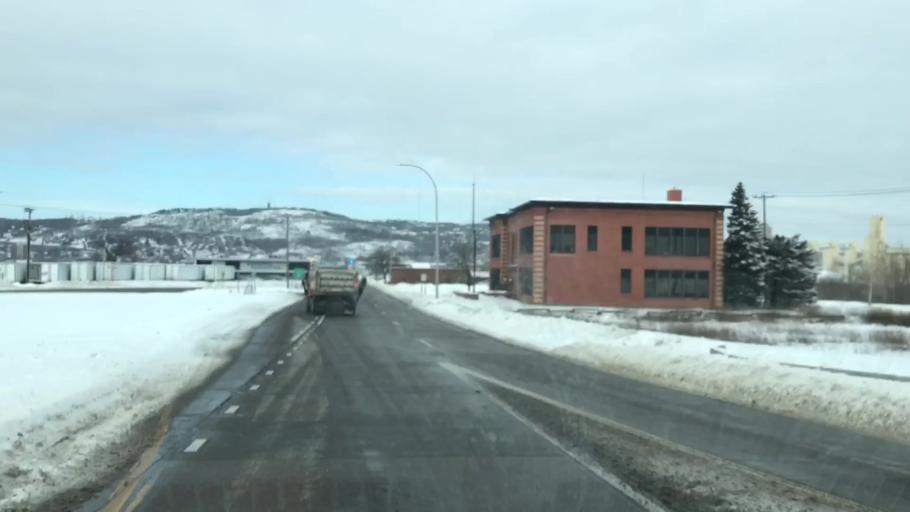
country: US
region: Minnesota
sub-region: Saint Louis County
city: Duluth
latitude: 46.7578
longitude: -92.1077
